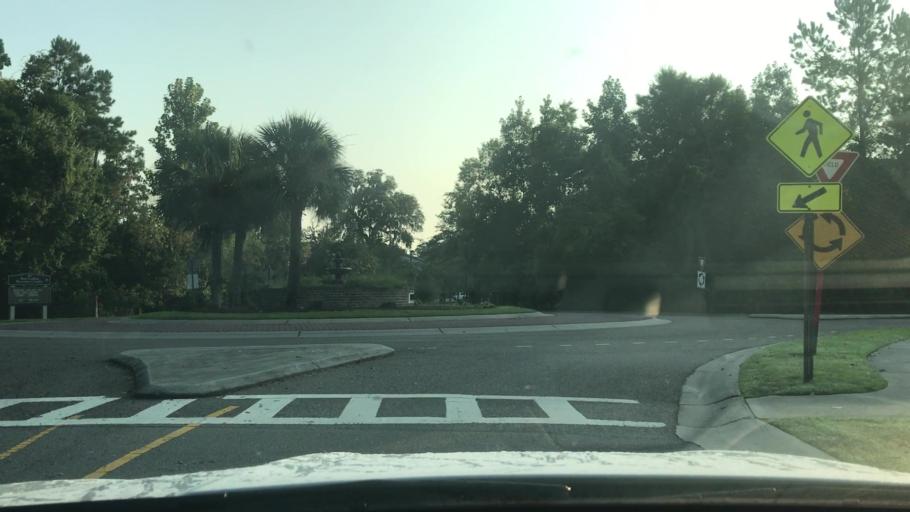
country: US
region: South Carolina
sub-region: Charleston County
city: Shell Point
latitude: 32.8310
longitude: -80.0963
